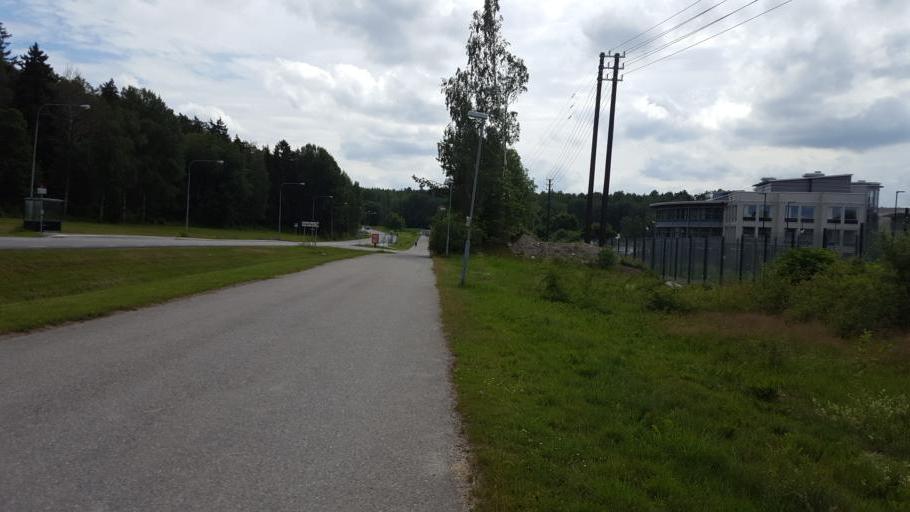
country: SE
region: Stockholm
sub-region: Upplands Vasby Kommun
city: Upplands Vaesby
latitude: 59.5106
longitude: 17.8996
